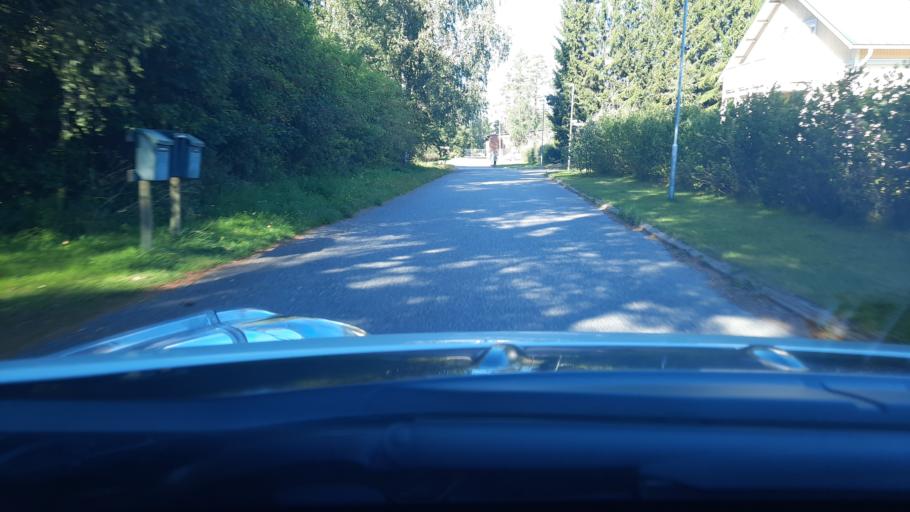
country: FI
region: North Karelia
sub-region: Joensuu
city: Joensuu
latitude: 62.6368
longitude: 29.6851
